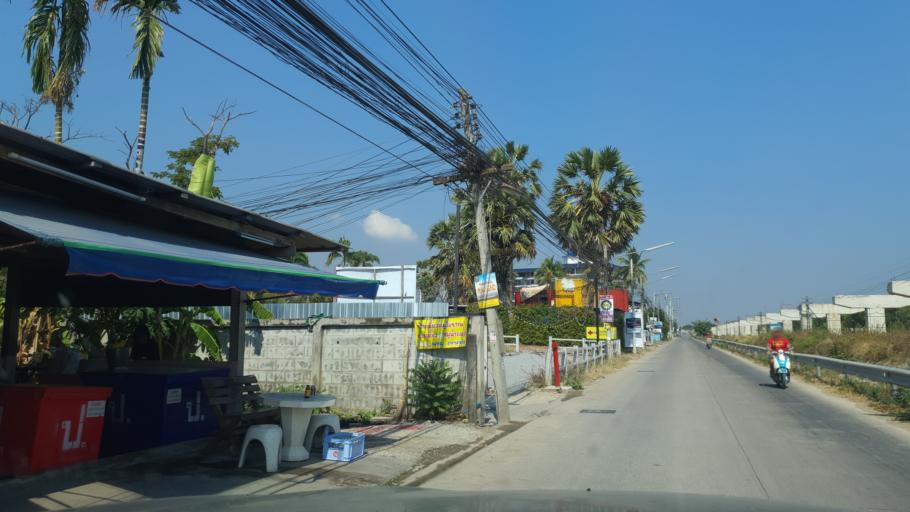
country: TH
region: Prachuap Khiri Khan
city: Hua Hin
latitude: 12.5551
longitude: 99.9574
